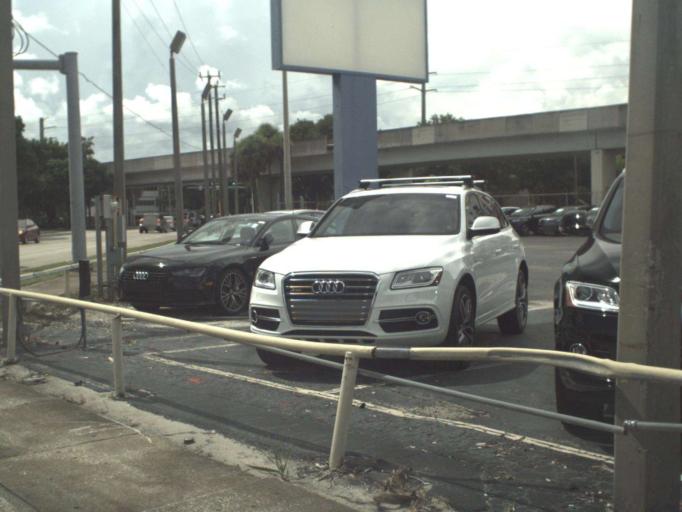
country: US
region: Florida
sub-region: Miami-Dade County
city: Coral Gables
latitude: 25.7276
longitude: -80.2603
